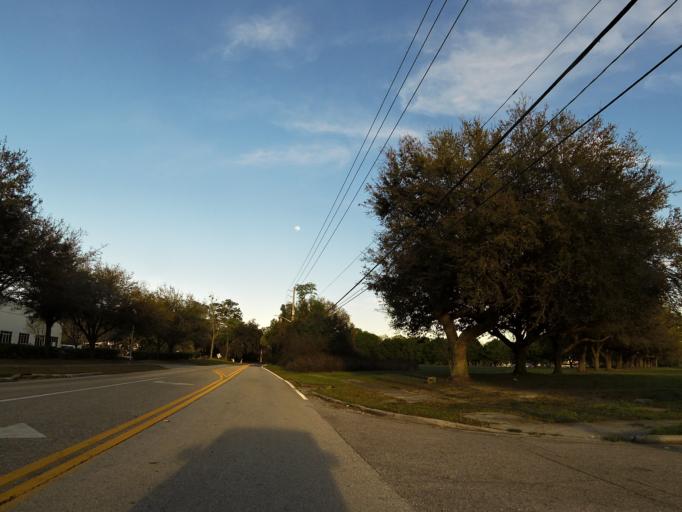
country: US
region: Florida
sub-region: Duval County
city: Jacksonville
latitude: 30.4676
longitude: -81.6597
